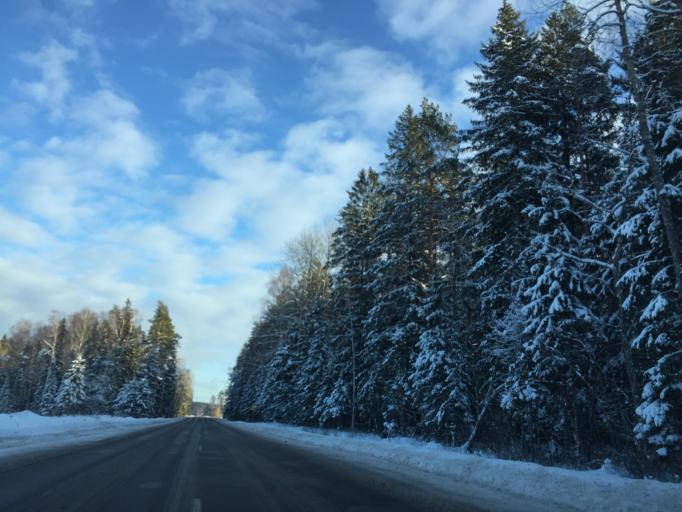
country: LV
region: Ropazu
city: Ropazi
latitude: 56.9523
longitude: 24.5337
